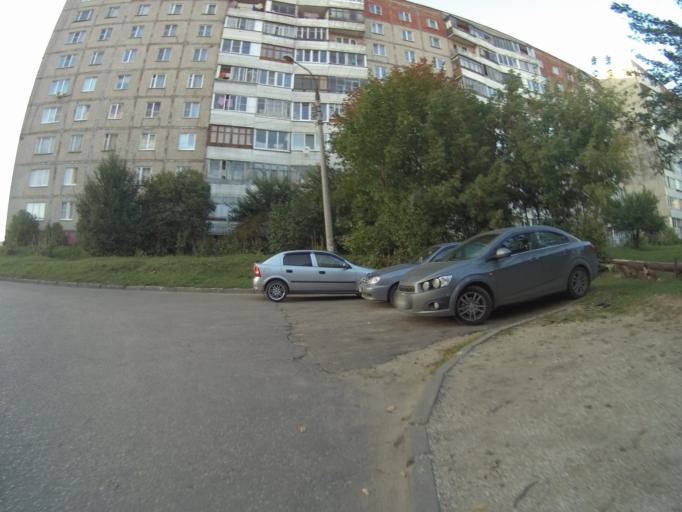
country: RU
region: Vladimir
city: Vladimir
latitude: 56.1086
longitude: 40.3491
